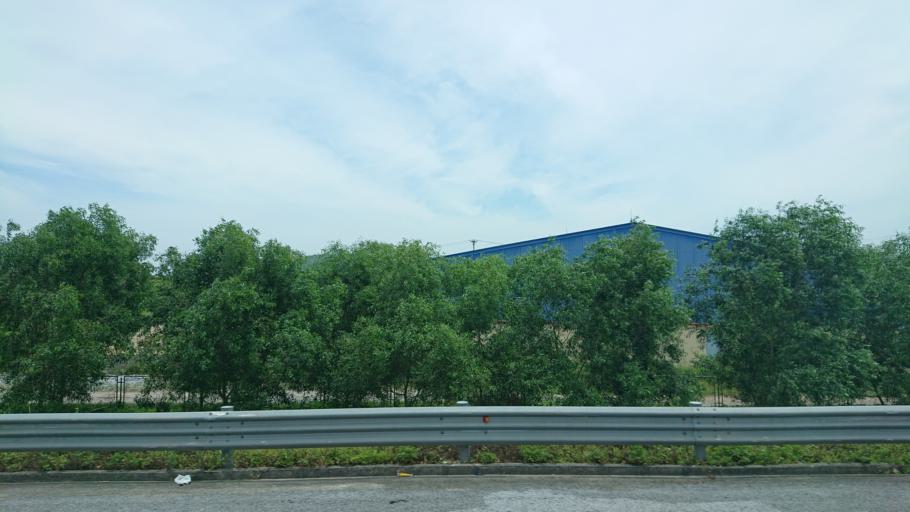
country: VN
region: Hai Phong
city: Nui Doi
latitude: 20.7707
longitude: 106.6167
